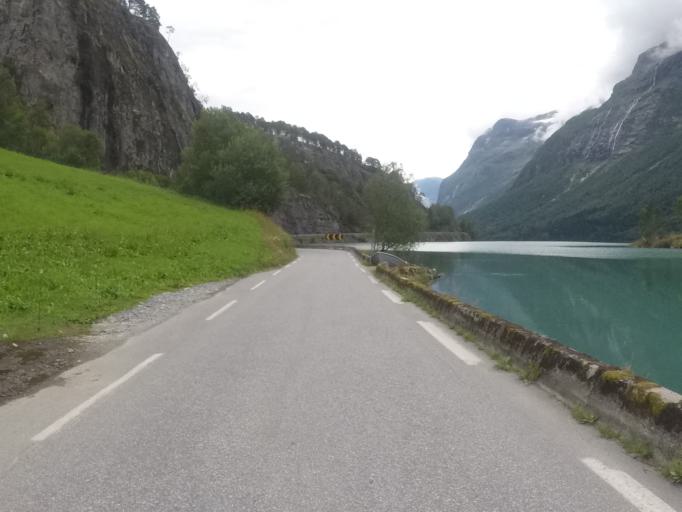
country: NO
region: Sogn og Fjordane
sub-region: Stryn
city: Stryn
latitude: 61.8597
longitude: 6.8907
